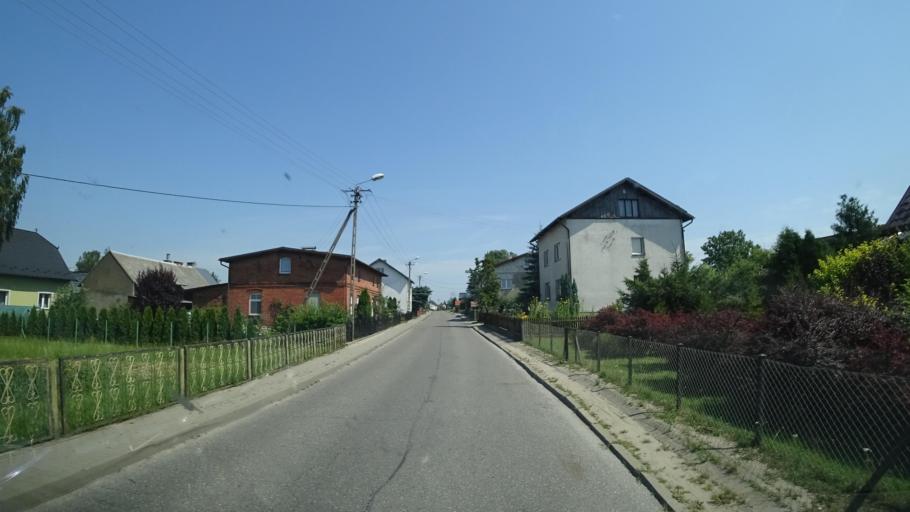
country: PL
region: Pomeranian Voivodeship
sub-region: Powiat chojnicki
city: Brusy
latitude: 53.8721
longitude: 17.6780
